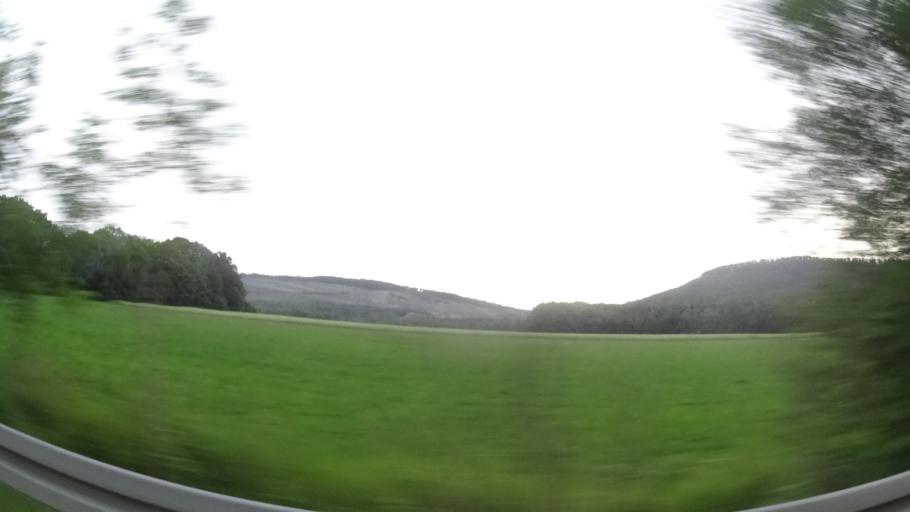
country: DE
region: Lower Saxony
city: Heyen
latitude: 52.0585
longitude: 9.5282
